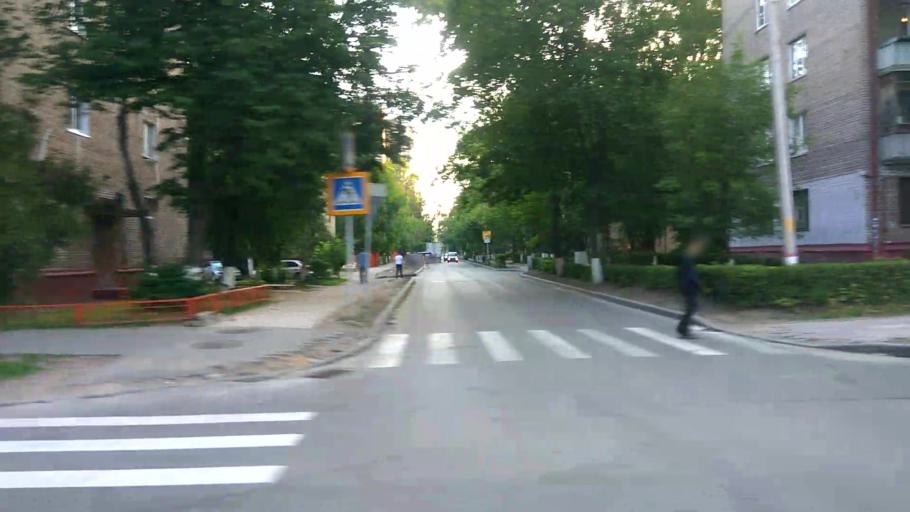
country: RU
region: Moskovskaya
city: Korolev
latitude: 55.9168
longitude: 37.8128
